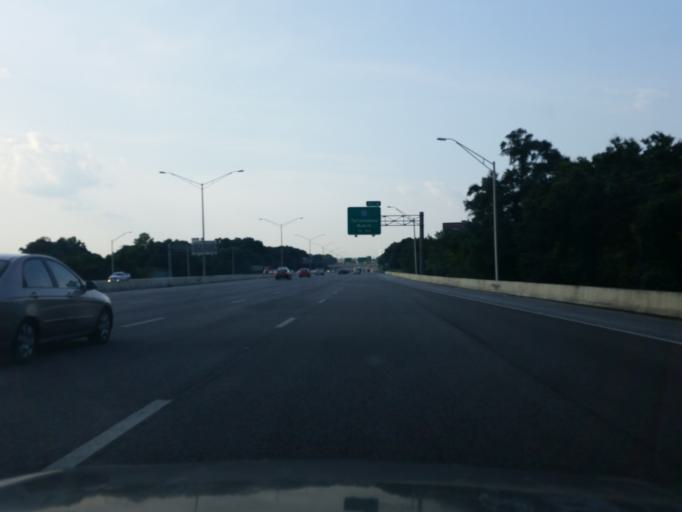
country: US
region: Florida
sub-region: Escambia County
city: Brent
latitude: 30.4875
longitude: -87.2301
